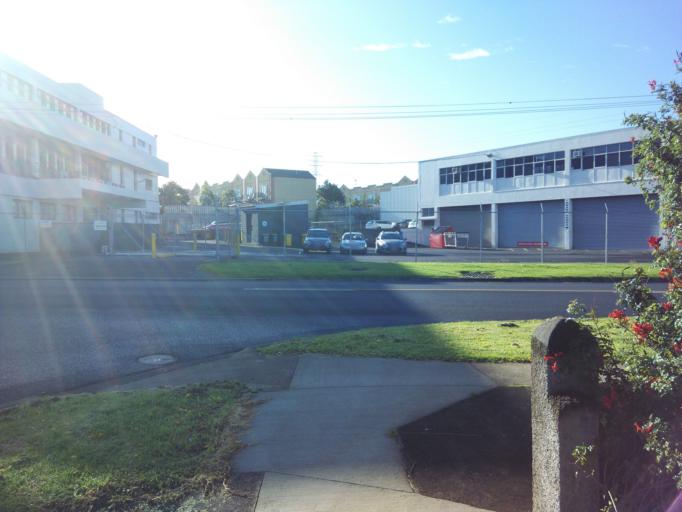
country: NZ
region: Auckland
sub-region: Auckland
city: Mangere
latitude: -36.9201
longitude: 174.7999
